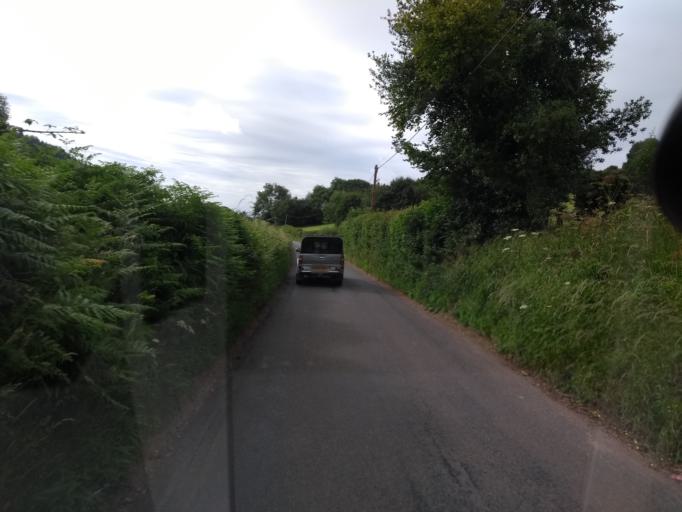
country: GB
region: England
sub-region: Somerset
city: Wiveliscombe
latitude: 51.0965
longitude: -3.3039
